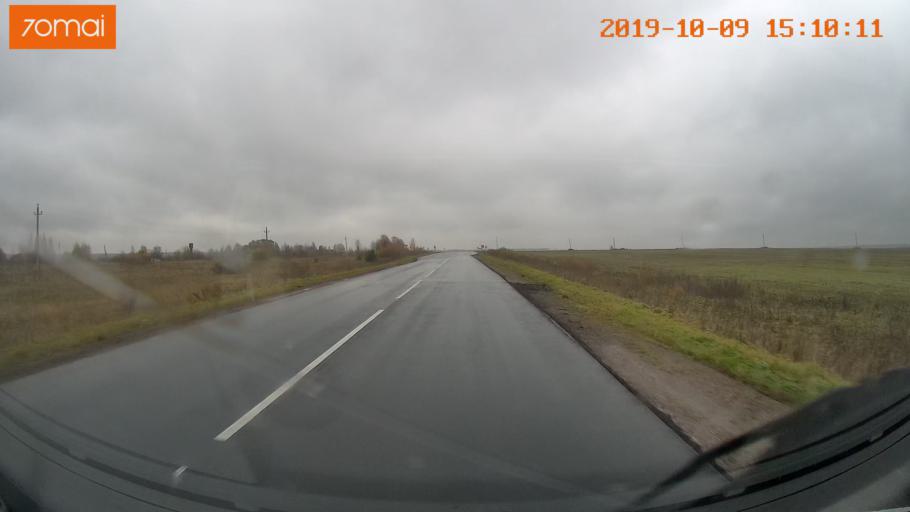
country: RU
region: Kostroma
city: Susanino
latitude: 58.1812
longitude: 41.6436
